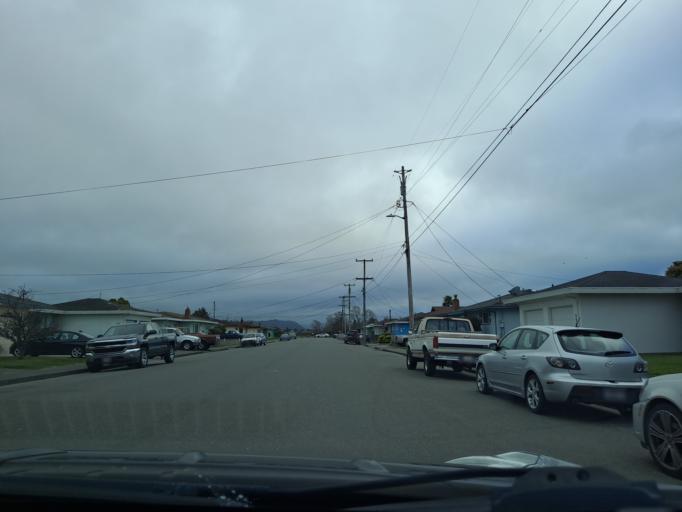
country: US
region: California
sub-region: Humboldt County
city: Fortuna
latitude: 40.5901
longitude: -124.1514
